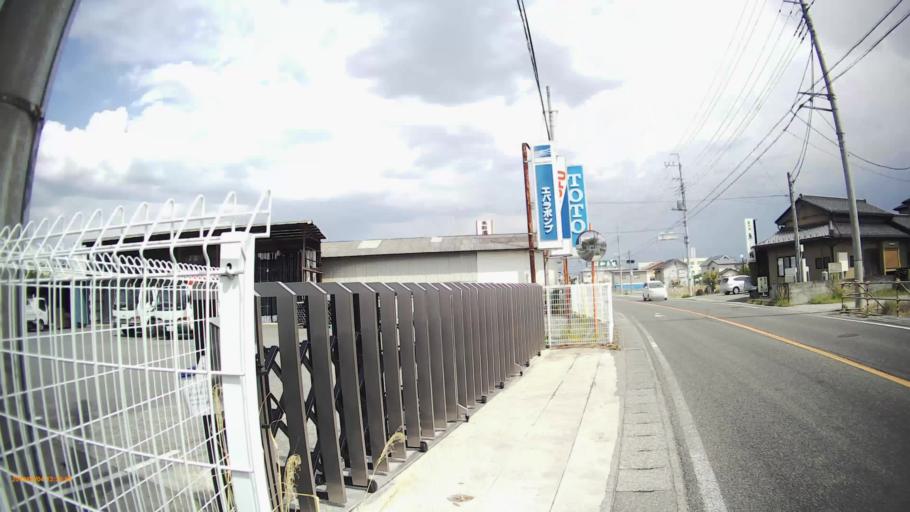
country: JP
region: Yamanashi
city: Ryuo
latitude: 35.6651
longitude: 138.5223
